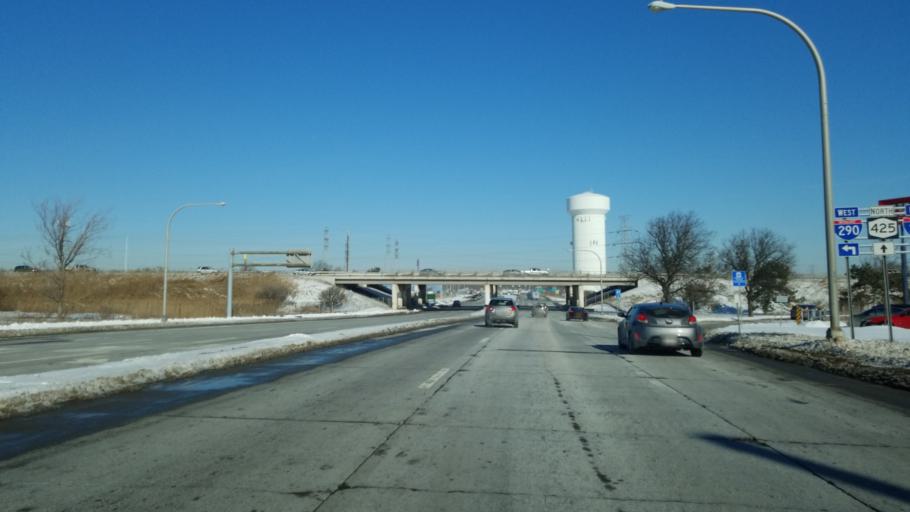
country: US
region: New York
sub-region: Erie County
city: Tonawanda
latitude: 42.9988
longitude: -78.8521
